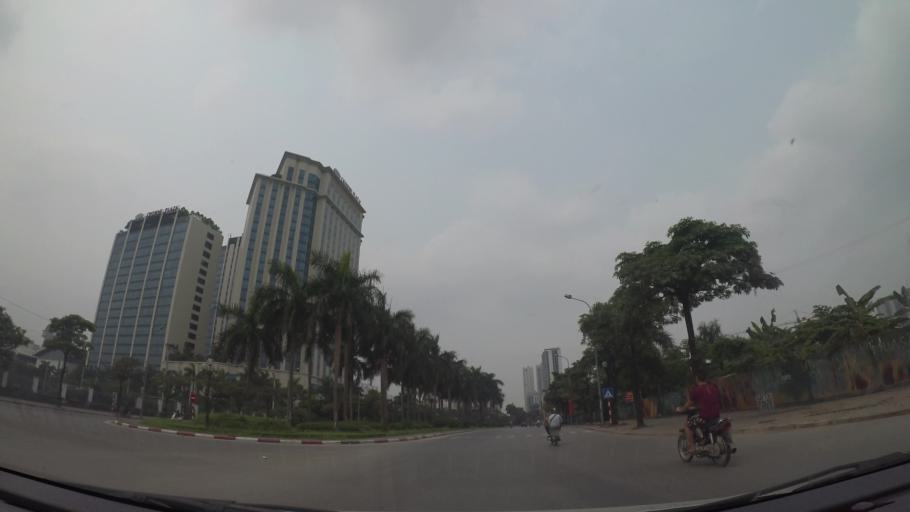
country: VN
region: Ha Noi
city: Cau Dien
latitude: 21.0261
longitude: 105.7679
